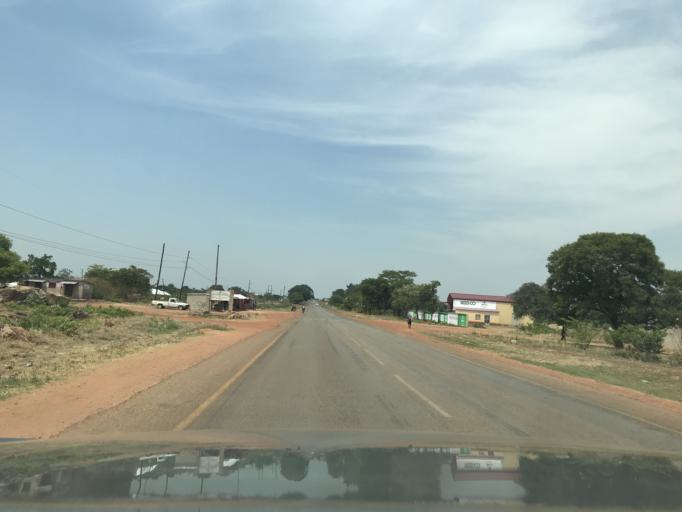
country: ZM
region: Northern
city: Kasama
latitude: -10.2155
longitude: 31.1502
